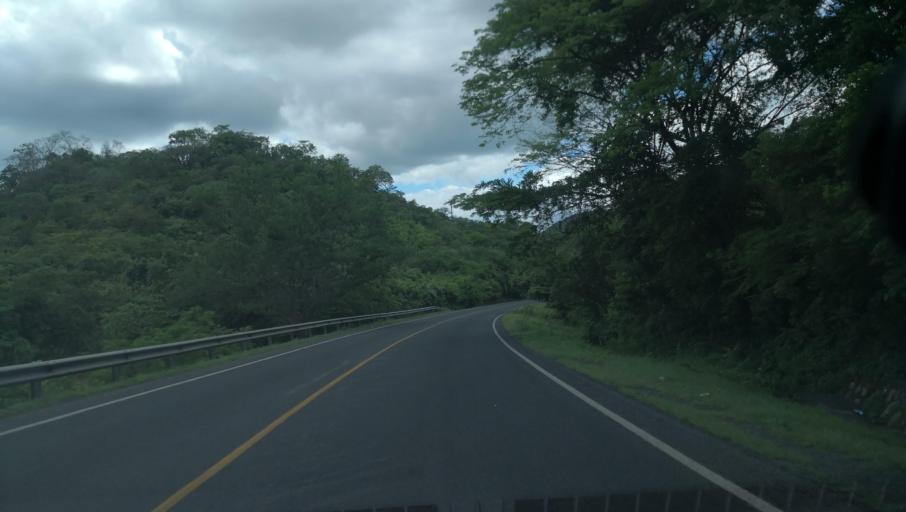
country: NI
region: Madriz
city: Palacaguina
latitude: 13.4454
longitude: -86.4417
